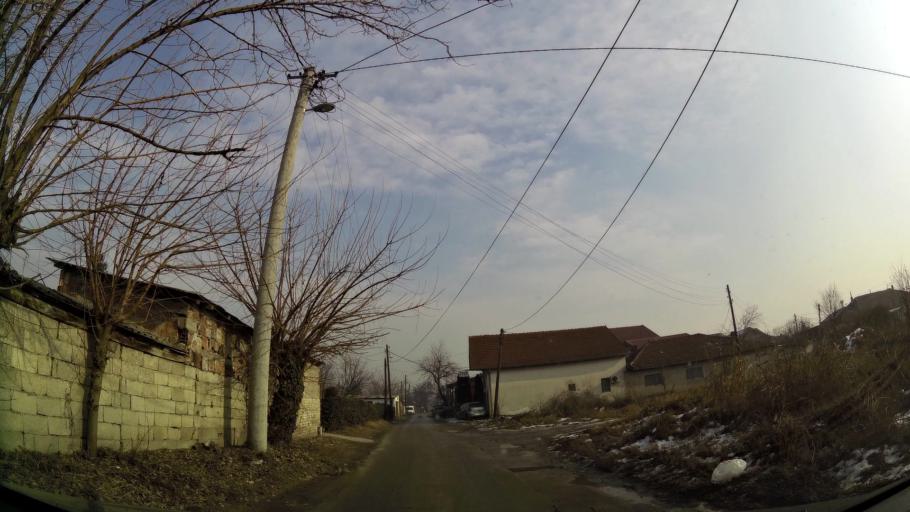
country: MK
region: Kisela Voda
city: Kisela Voda
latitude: 41.9964
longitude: 21.4945
